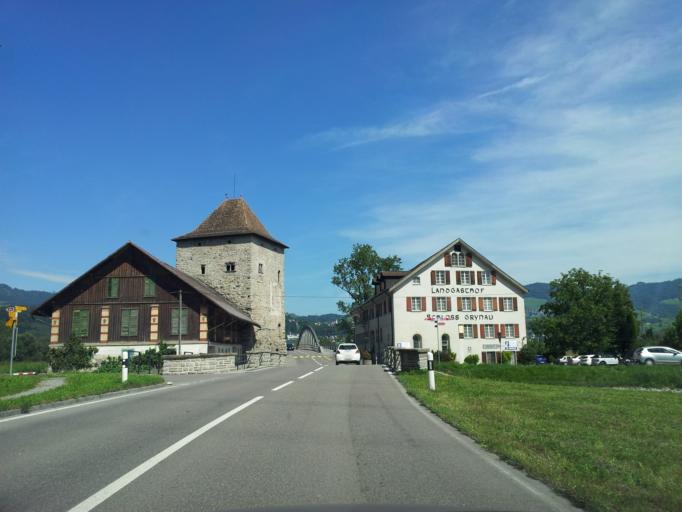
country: CH
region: Saint Gallen
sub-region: Wahlkreis See-Gaster
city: Uznach
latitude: 47.2158
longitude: 8.9694
